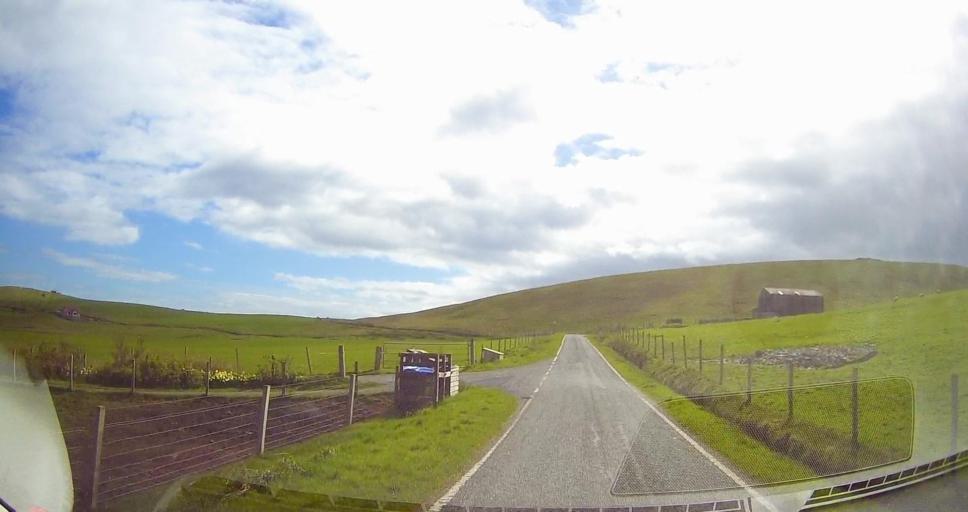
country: GB
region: Scotland
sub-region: Shetland Islands
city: Sandwick
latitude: 59.9291
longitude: -1.3452
